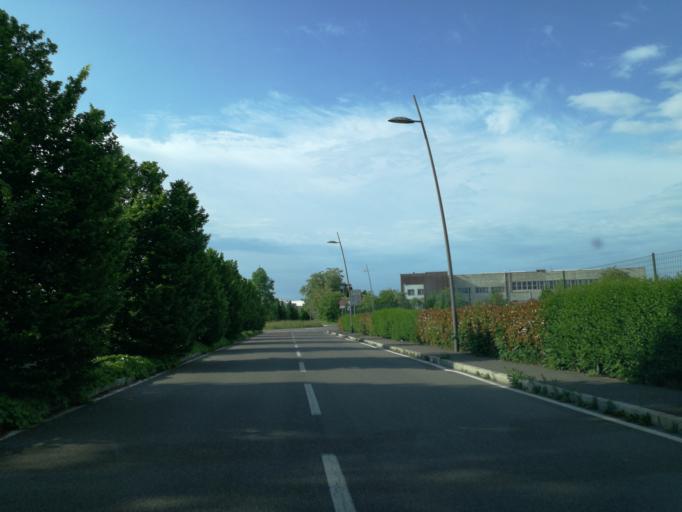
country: IT
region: Lombardy
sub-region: Provincia di Monza e Brianza
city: Vimercate
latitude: 45.6074
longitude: 9.3592
